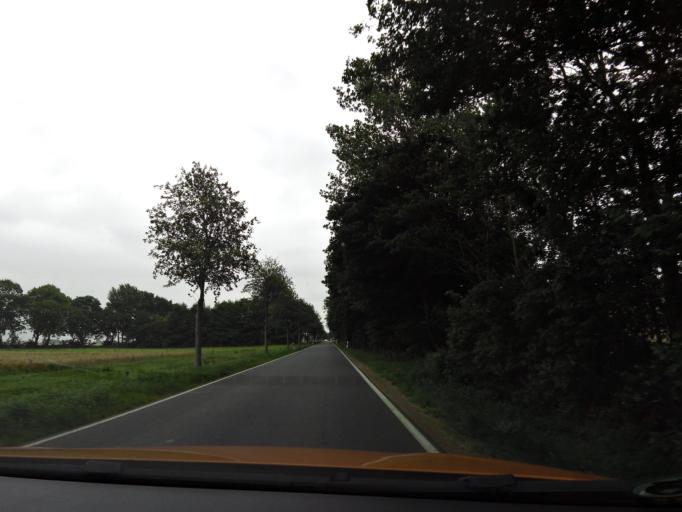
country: DE
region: Lower Saxony
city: Wirdum
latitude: 53.5107
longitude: 7.1456
